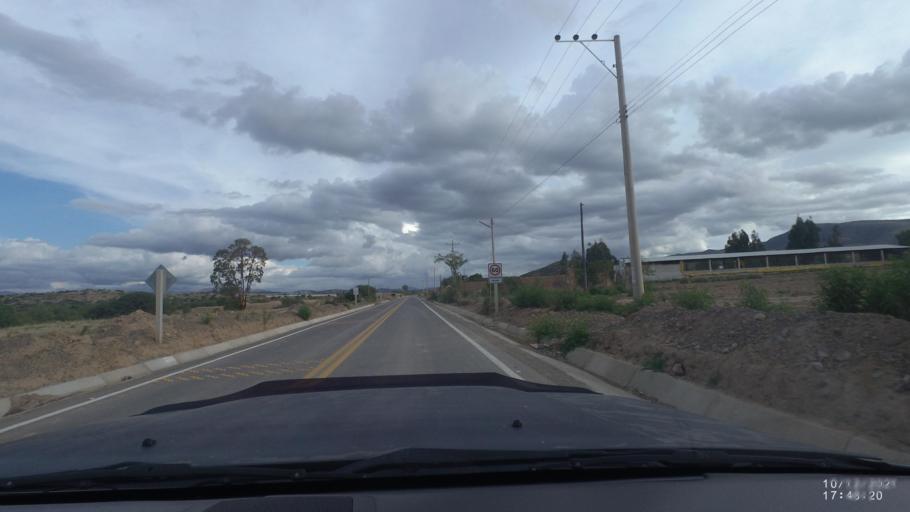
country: BO
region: Cochabamba
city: Tarata
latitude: -17.6451
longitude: -65.9785
